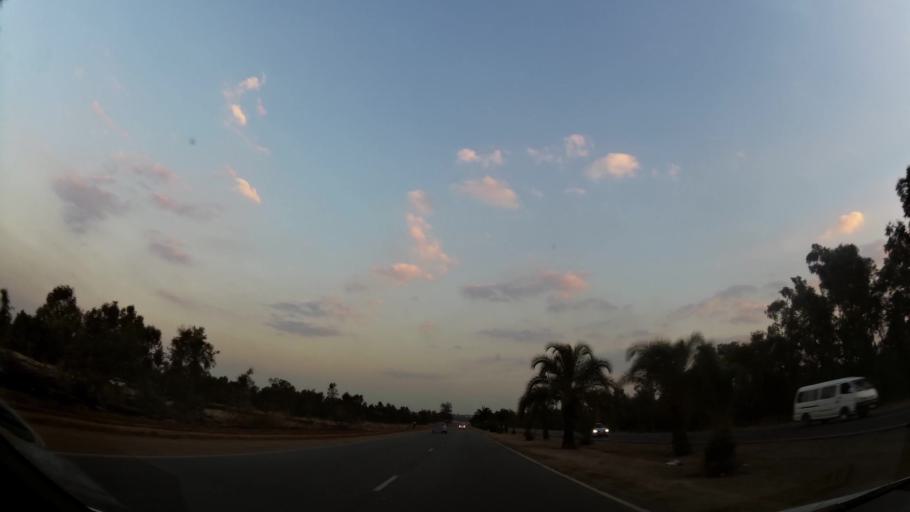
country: ZA
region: Gauteng
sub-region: Ekurhuleni Metropolitan Municipality
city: Springs
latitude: -26.2735
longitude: 28.4293
